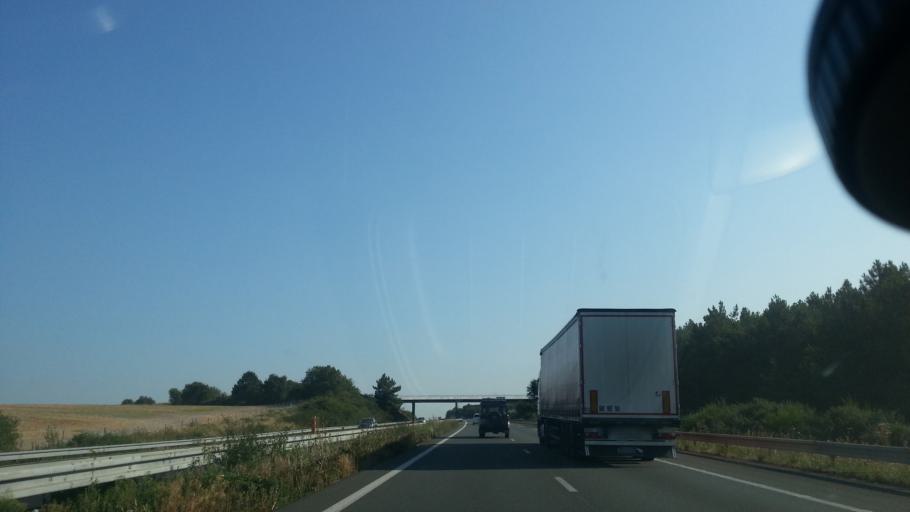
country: FR
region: Poitou-Charentes
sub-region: Departement de la Vienne
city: Dange-Saint-Romain
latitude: 46.9270
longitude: 0.5388
